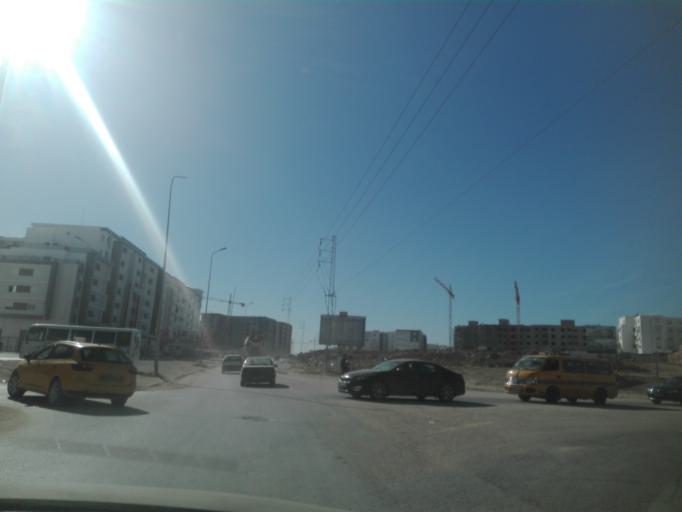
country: TN
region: Bin 'Arus
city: Ben Arous
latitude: 36.7134
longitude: 10.2151
